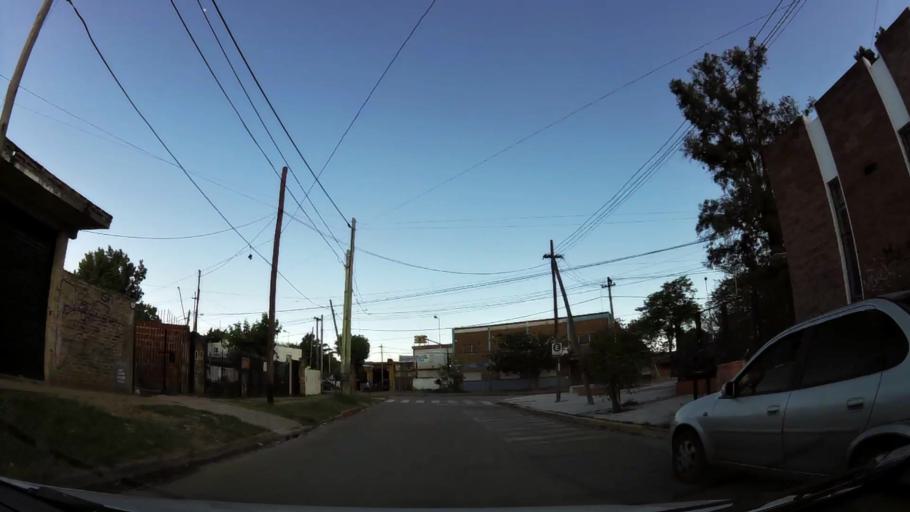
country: AR
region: Buenos Aires
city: Ituzaingo
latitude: -34.6939
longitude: -58.6394
